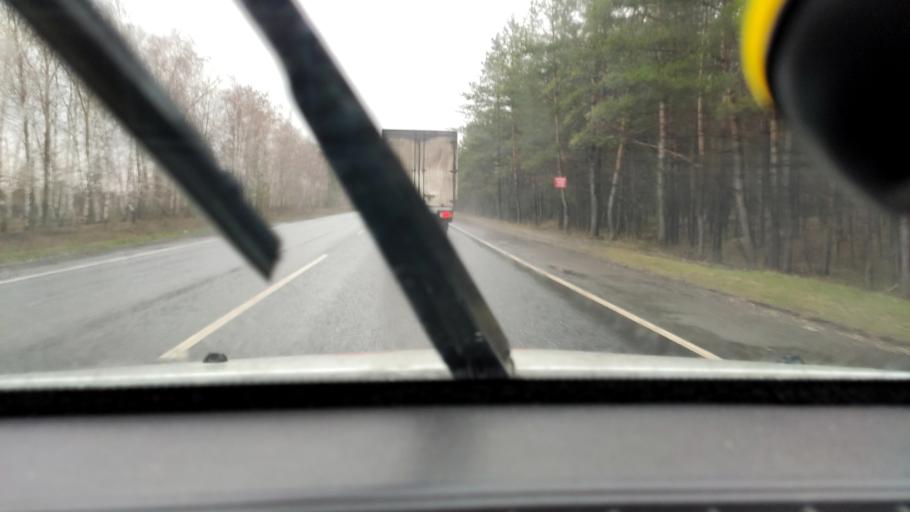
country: RU
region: Samara
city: Povolzhskiy
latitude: 53.6127
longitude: 49.6222
